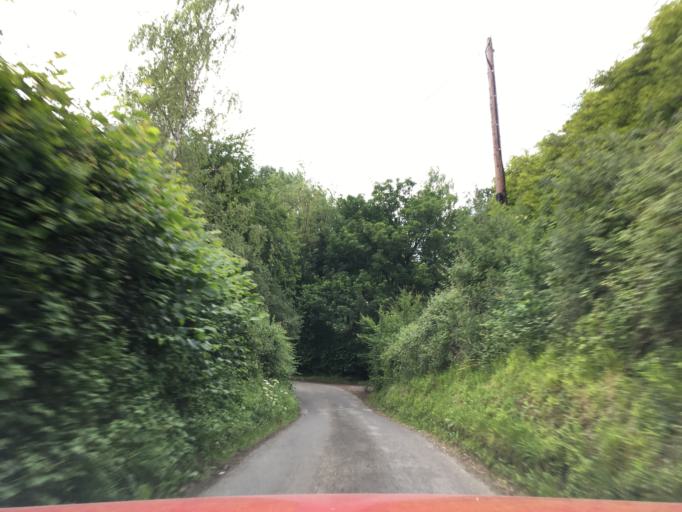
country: GB
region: England
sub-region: South Gloucestershire
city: Horton
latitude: 51.5751
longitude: -2.3497
